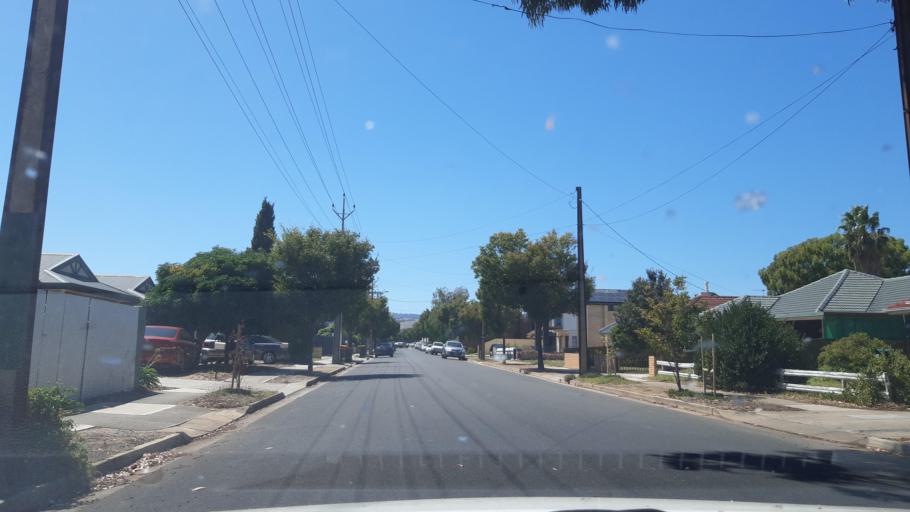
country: AU
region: South Australia
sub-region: Marion
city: Clovelly Park
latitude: -34.9879
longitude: 138.5682
